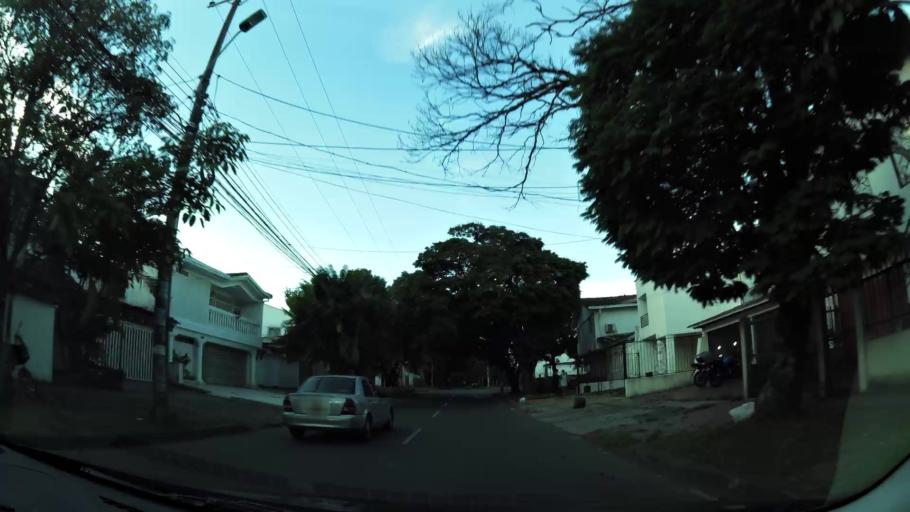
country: CO
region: Valle del Cauca
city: Cali
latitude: 3.4064
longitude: -76.5497
